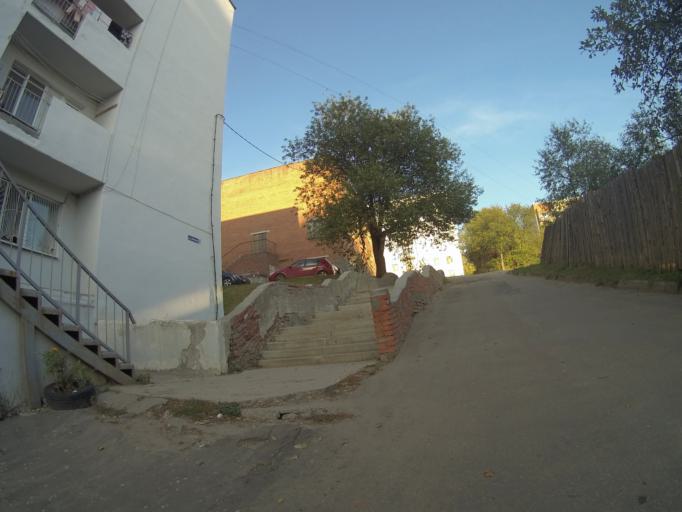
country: RU
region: Vladimir
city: Vladimir
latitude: 56.1089
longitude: 40.3712
